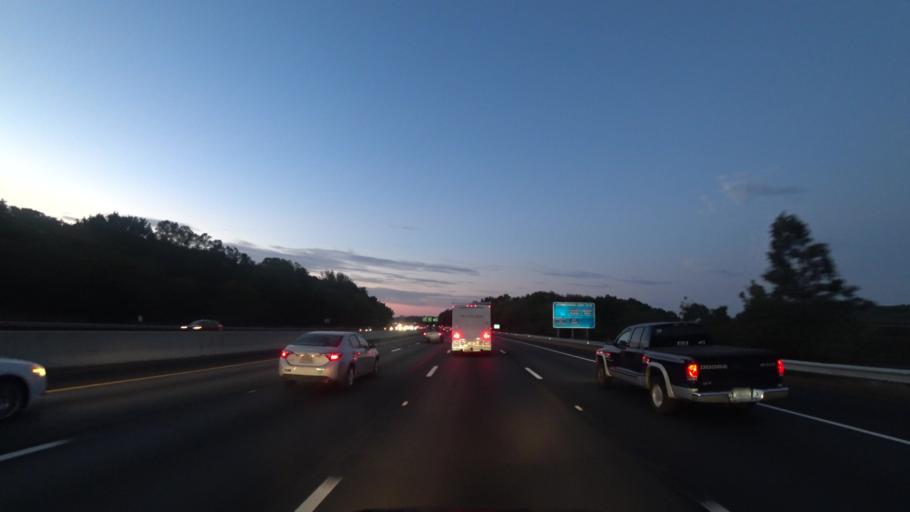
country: US
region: Massachusetts
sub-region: Middlesex County
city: Lexington
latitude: 42.4359
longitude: -71.2599
